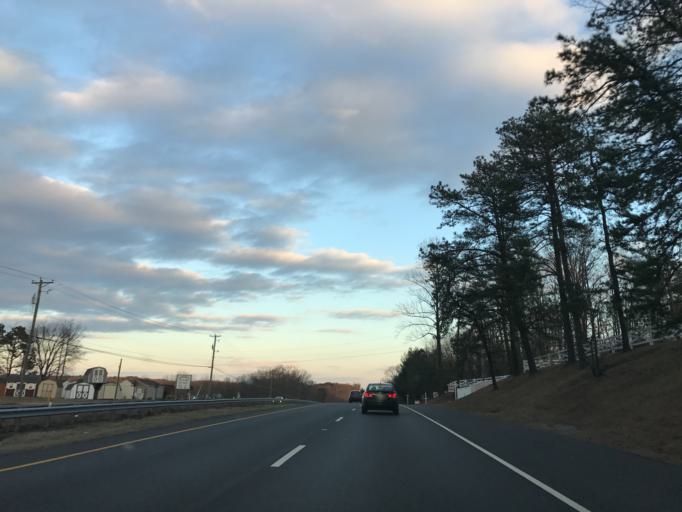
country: US
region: Maryland
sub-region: Cecil County
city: North East
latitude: 39.6098
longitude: -75.8975
